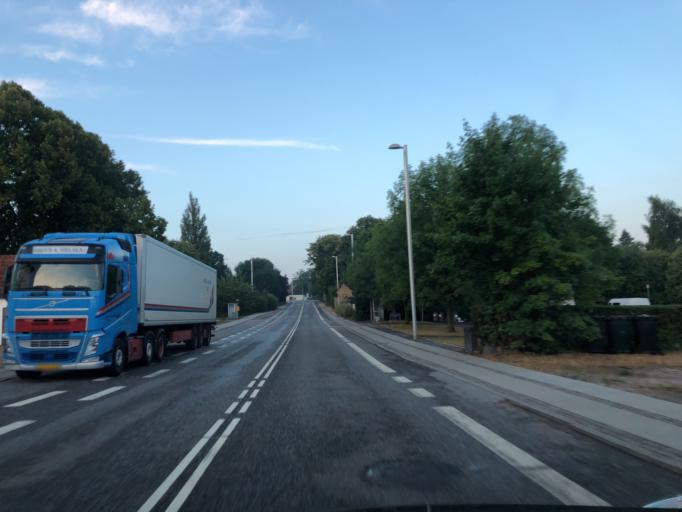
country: DK
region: Zealand
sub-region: Holbaek Kommune
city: Vipperod
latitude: 55.6525
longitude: 11.6686
